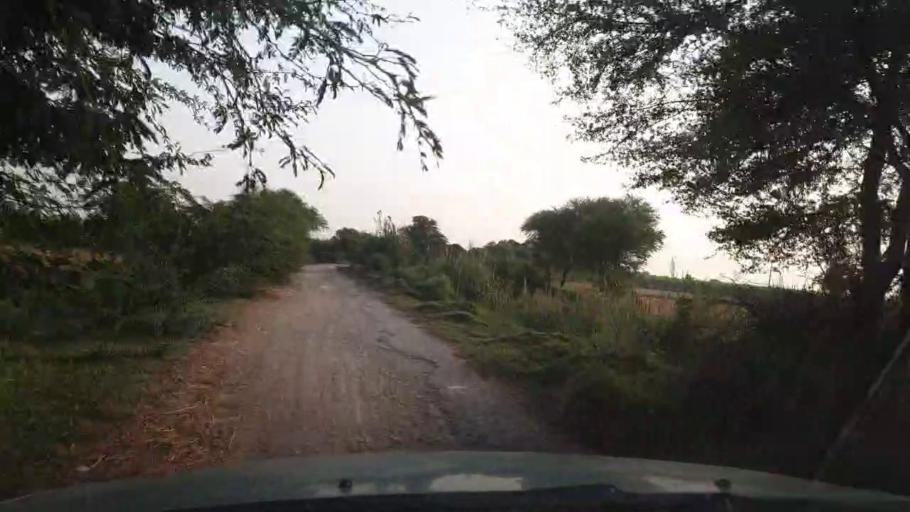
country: PK
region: Sindh
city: Tando Muhammad Khan
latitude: 25.0044
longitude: 68.4353
